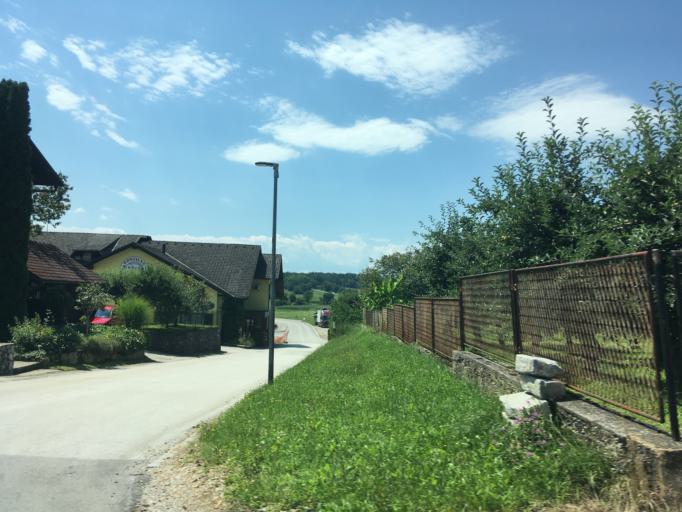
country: SI
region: Metlika
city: Metlika
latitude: 45.6434
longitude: 15.3200
